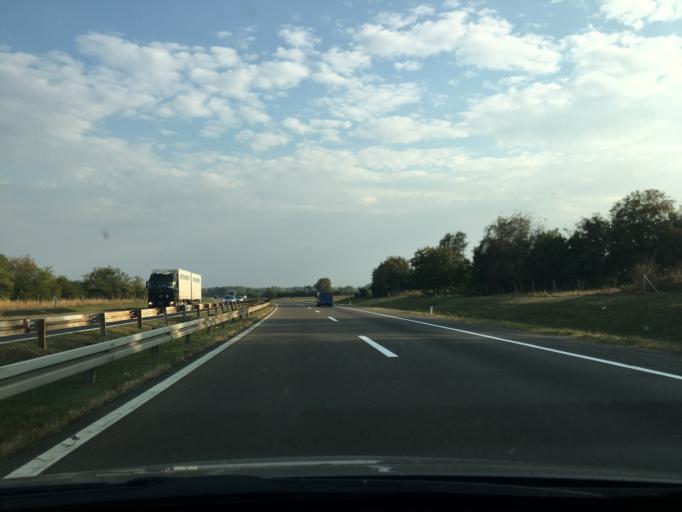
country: RS
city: Lugavcina
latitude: 44.5465
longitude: 20.9868
